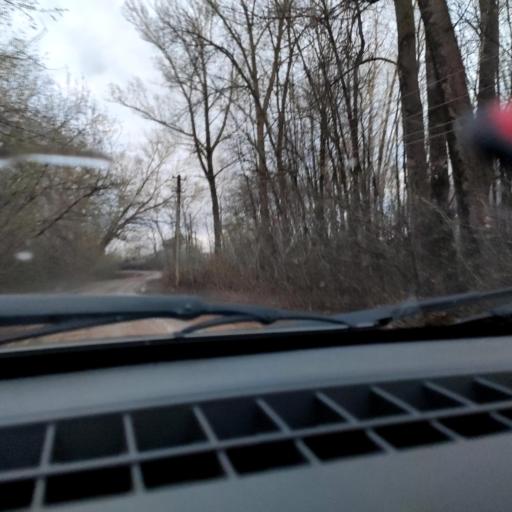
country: RU
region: Bashkortostan
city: Ufa
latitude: 54.6741
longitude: 55.9520
